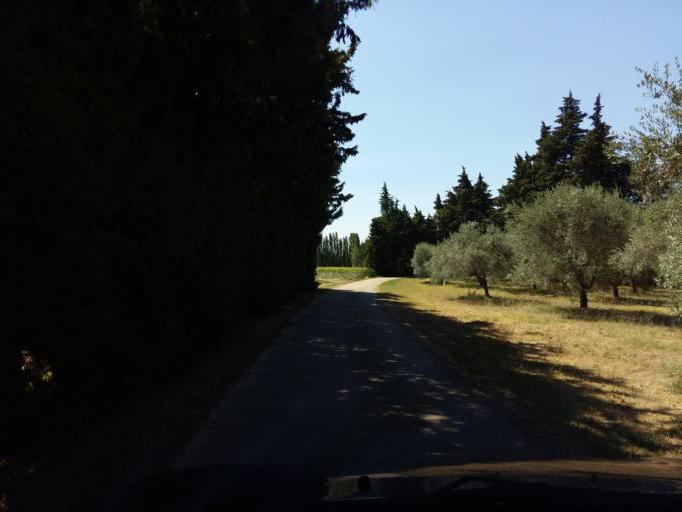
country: FR
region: Provence-Alpes-Cote d'Azur
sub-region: Departement du Vaucluse
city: Loriol-du-Comtat
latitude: 44.0891
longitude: 5.0030
